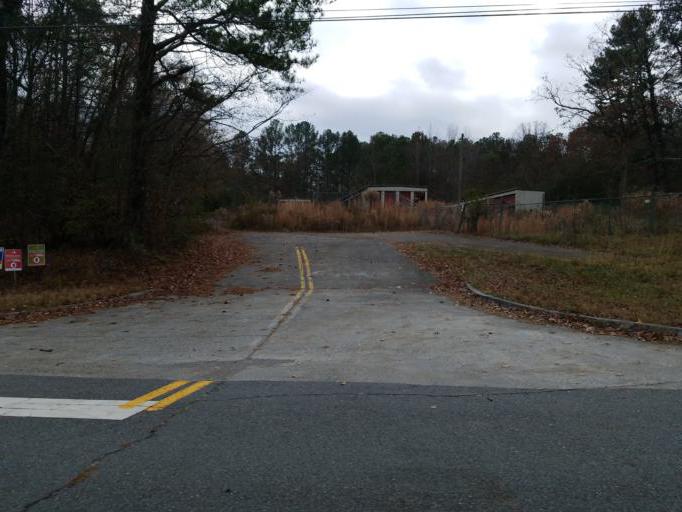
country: US
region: Georgia
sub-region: Cherokee County
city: Canton
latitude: 34.2130
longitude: -84.5302
